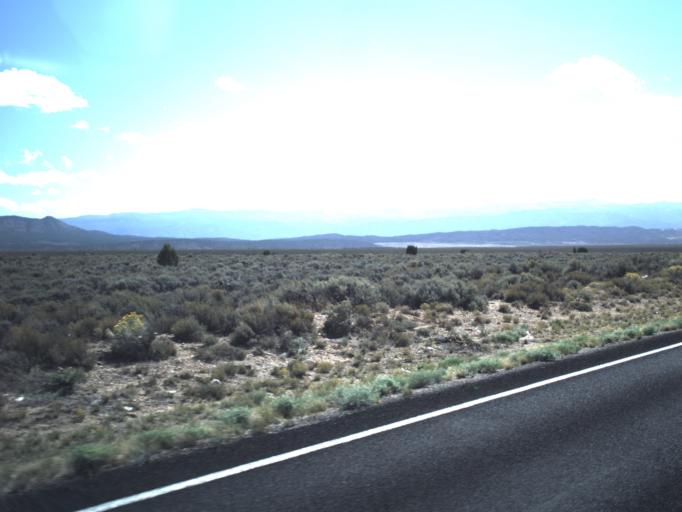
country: US
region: Utah
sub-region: Iron County
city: Enoch
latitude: 38.0086
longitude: -112.9979
